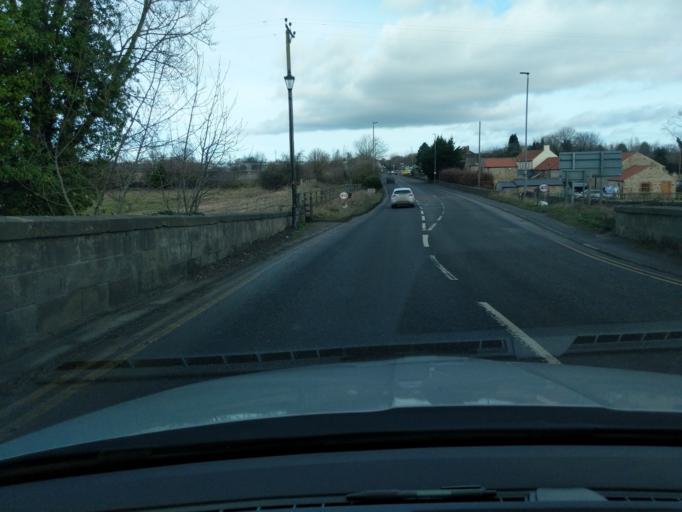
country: GB
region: England
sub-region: North Yorkshire
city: Catterick
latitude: 54.3895
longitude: -1.6516
